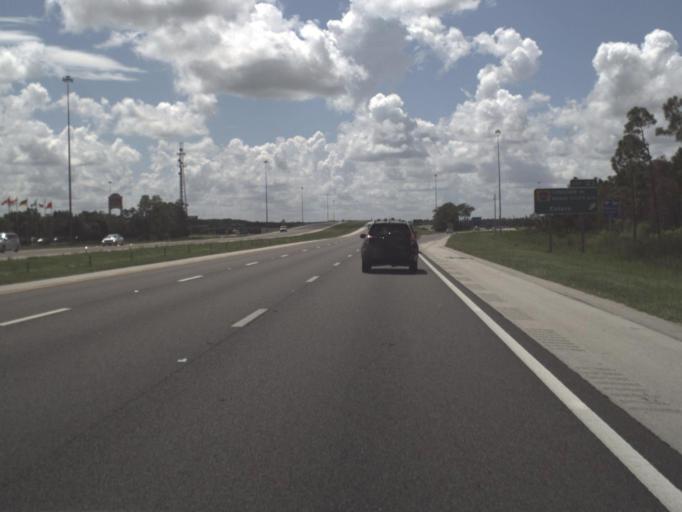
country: US
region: Florida
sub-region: Lee County
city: Estero
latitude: 26.4382
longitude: -81.7802
